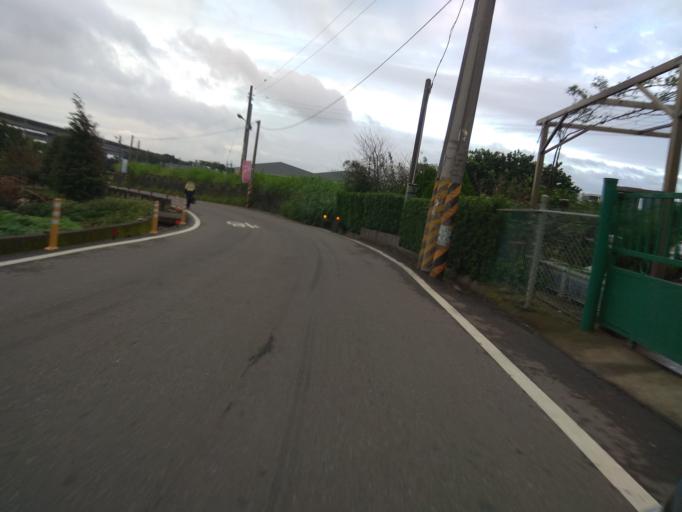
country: TW
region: Taiwan
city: Daxi
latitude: 24.9390
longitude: 121.1947
